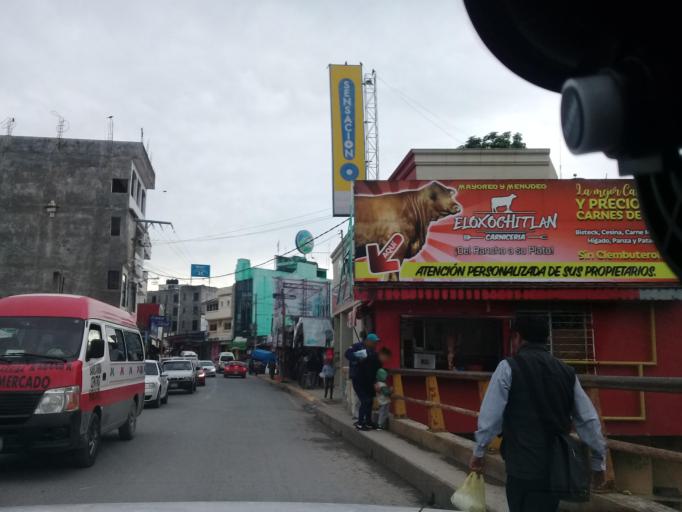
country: MX
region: Hidalgo
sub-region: Huejutla de Reyes
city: Huejutla de Reyes
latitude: 21.1429
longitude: -98.4183
